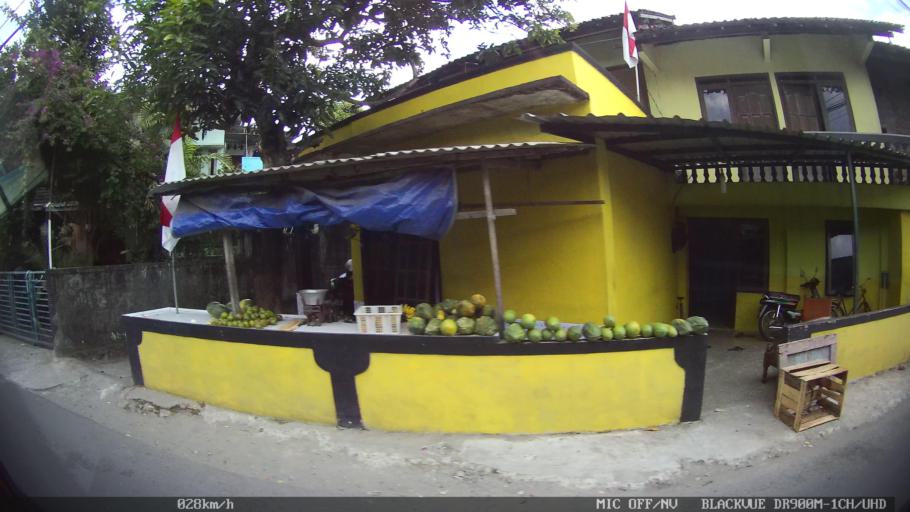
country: ID
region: Daerah Istimewa Yogyakarta
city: Gamping Lor
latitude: -7.7843
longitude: 110.3355
